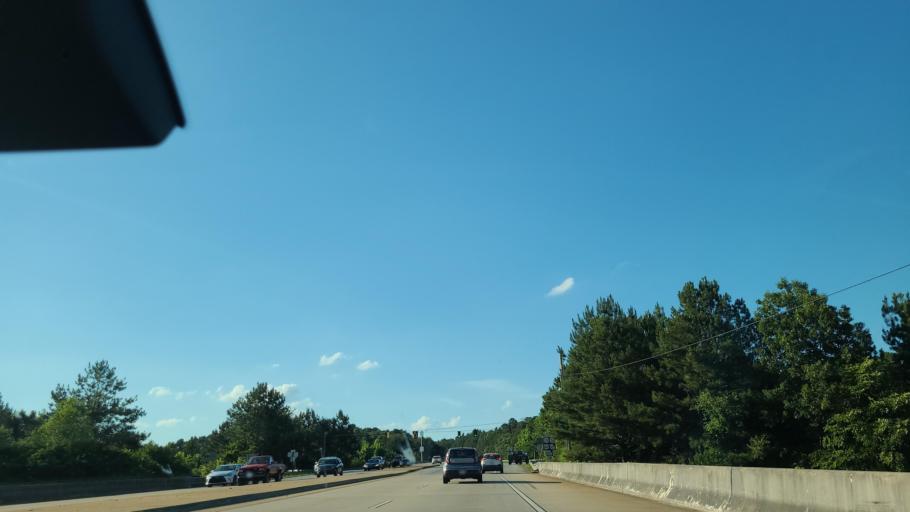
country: US
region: Georgia
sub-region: Oconee County
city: Watkinsville
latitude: 33.9137
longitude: -83.4048
